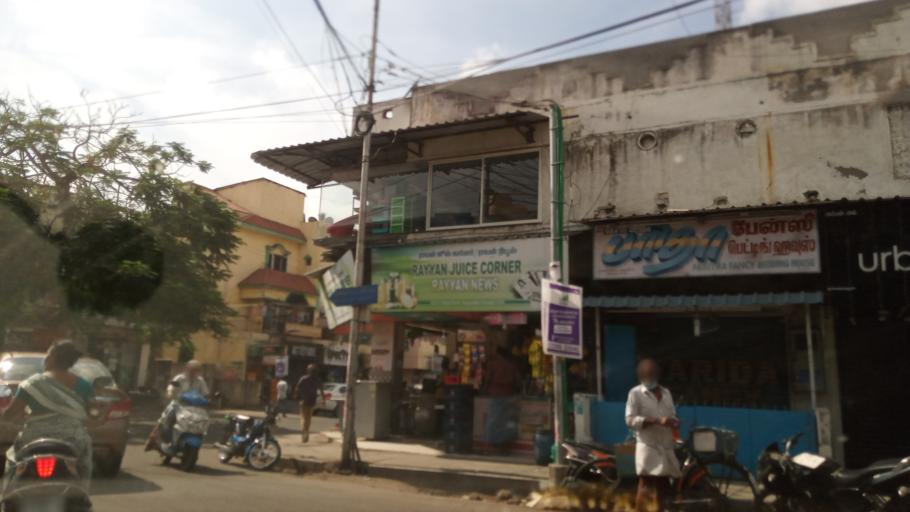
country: IN
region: Tamil Nadu
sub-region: Kancheepuram
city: Saint Thomas Mount
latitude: 12.9866
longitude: 80.1882
